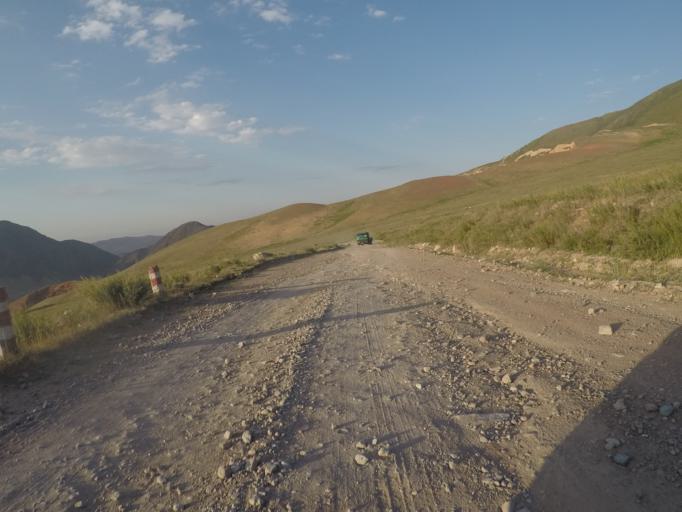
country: KG
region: Chuy
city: Bishkek
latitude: 42.6549
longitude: 74.6542
